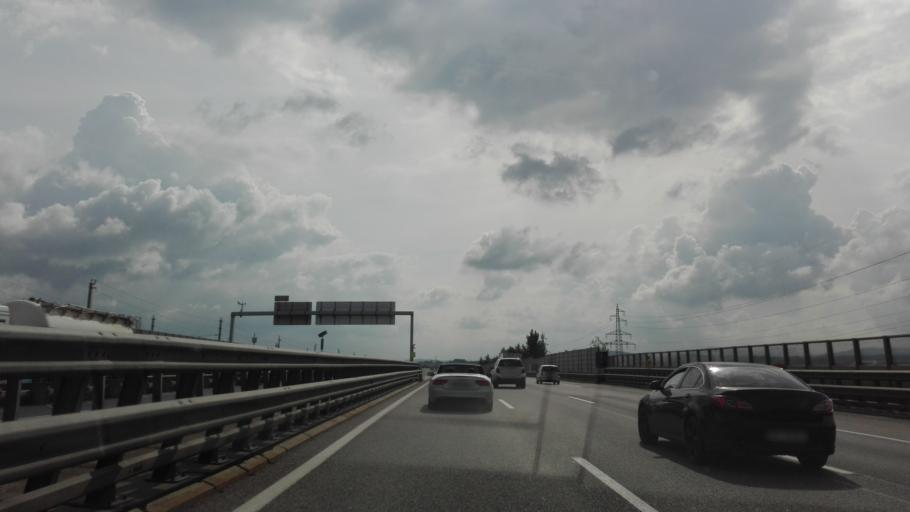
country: AT
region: Lower Austria
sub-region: Sankt Polten Stadt
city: Sankt Poelten
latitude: 48.1770
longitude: 15.6156
